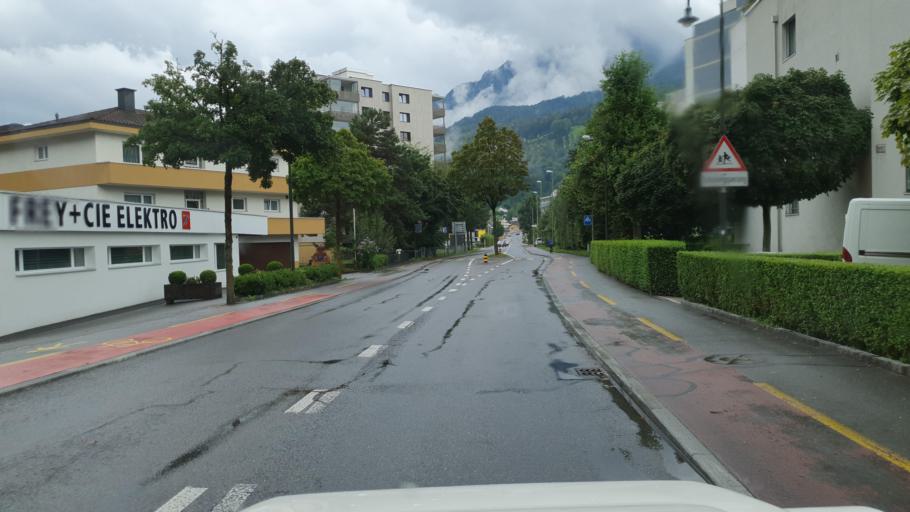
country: CH
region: Lucerne
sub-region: Lucerne-Land District
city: Horw
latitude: 47.0142
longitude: 8.3110
